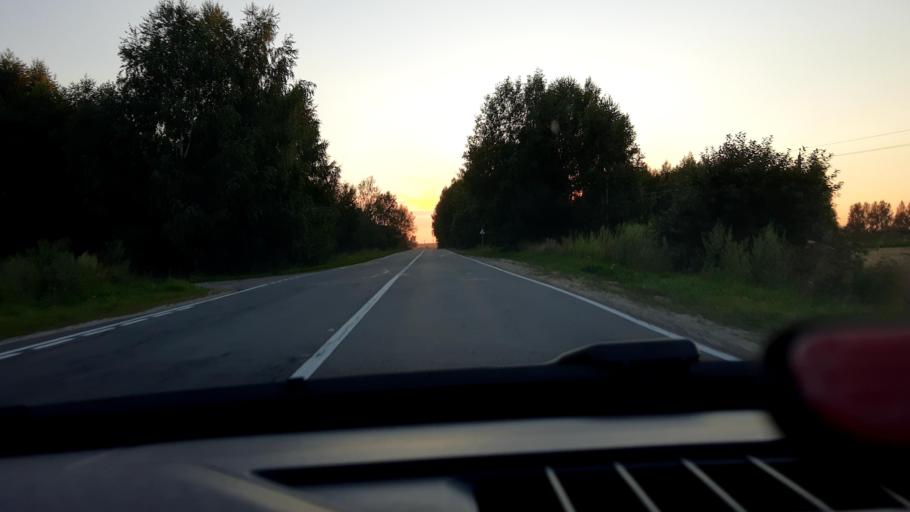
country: RU
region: Nizjnij Novgorod
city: Neklyudovo
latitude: 56.5233
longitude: 43.8713
